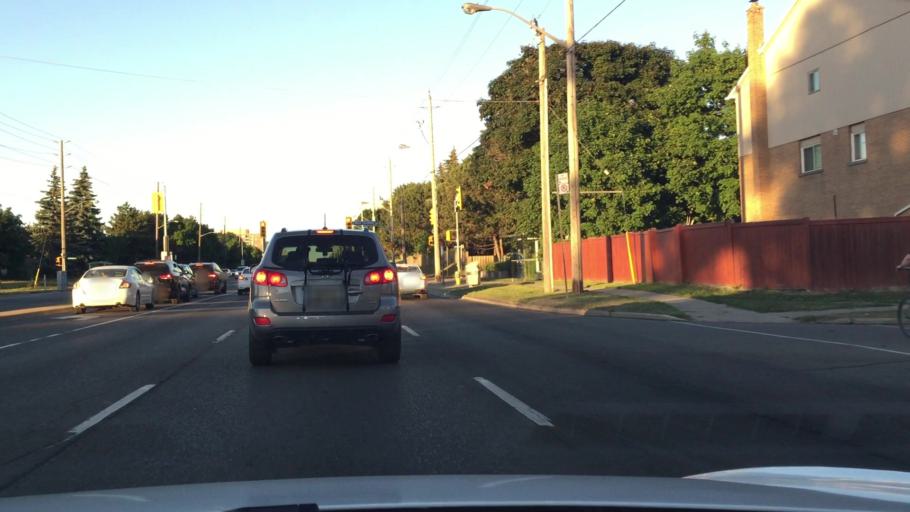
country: CA
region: Ontario
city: Concord
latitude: 43.7896
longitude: -79.4584
